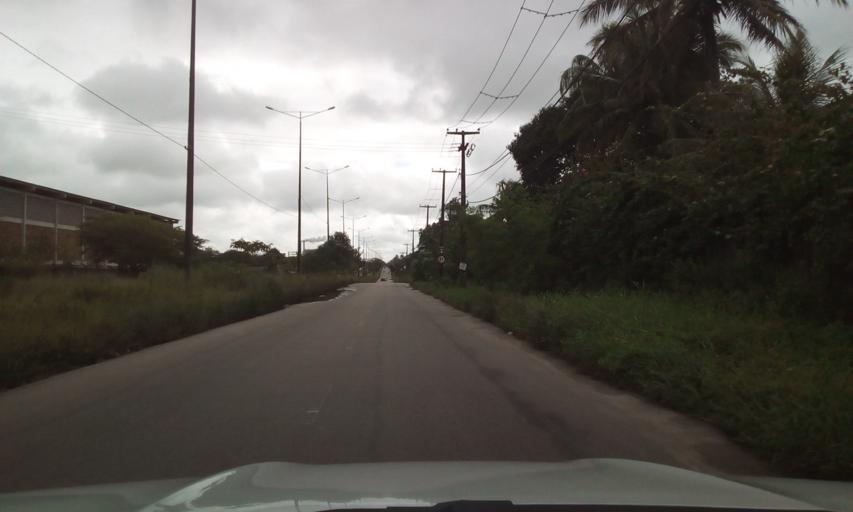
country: BR
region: Paraiba
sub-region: Bayeux
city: Bayeux
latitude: -7.1802
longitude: -34.9012
